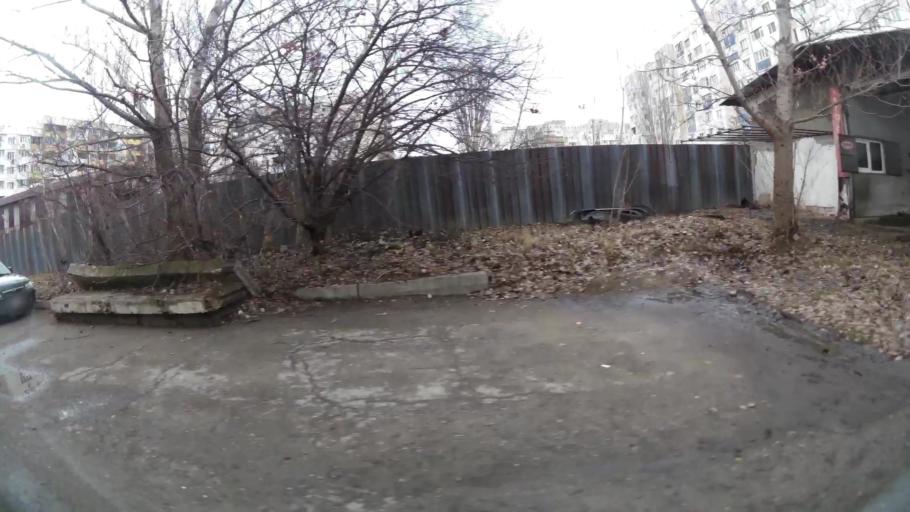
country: BG
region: Sofia-Capital
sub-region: Stolichna Obshtina
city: Sofia
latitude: 42.7361
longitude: 23.2892
